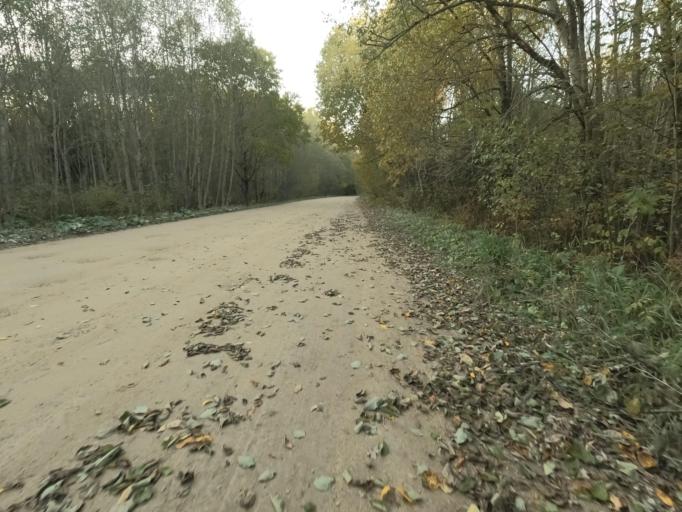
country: RU
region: Leningrad
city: Lyuban'
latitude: 59.0035
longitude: 31.0971
